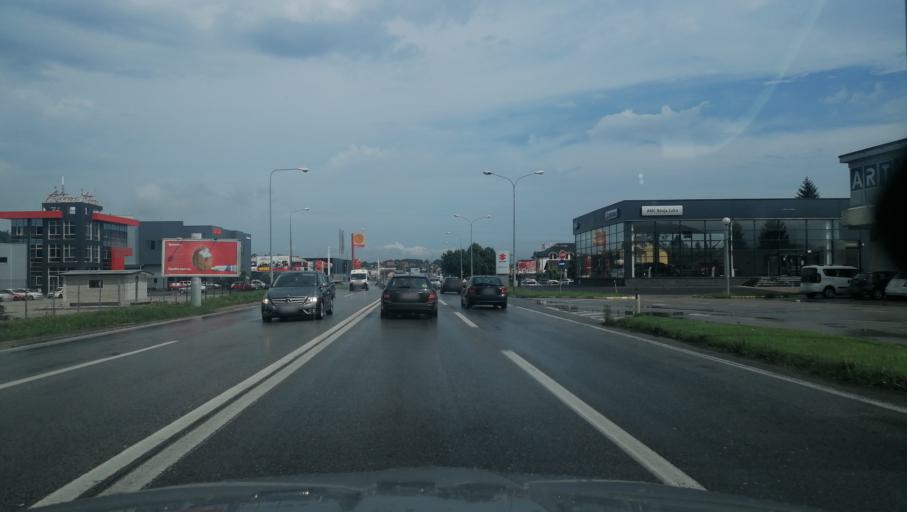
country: BA
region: Republika Srpska
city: Banja Luka
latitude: 44.8035
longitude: 17.1984
